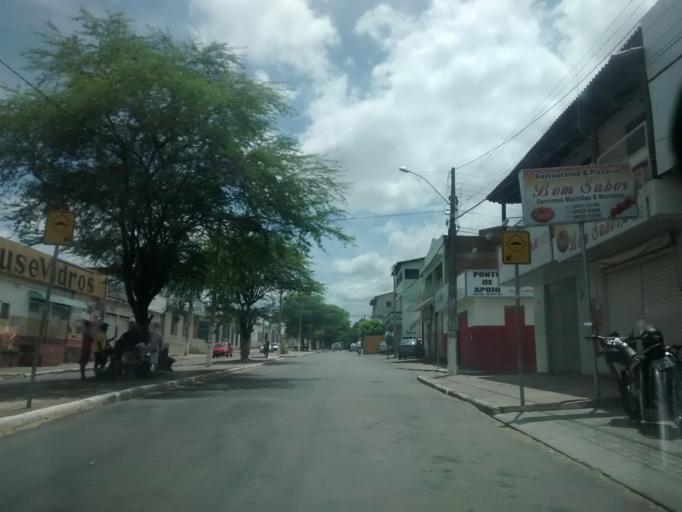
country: BR
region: Bahia
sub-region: Brumado
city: Brumado
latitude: -14.2126
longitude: -41.6750
